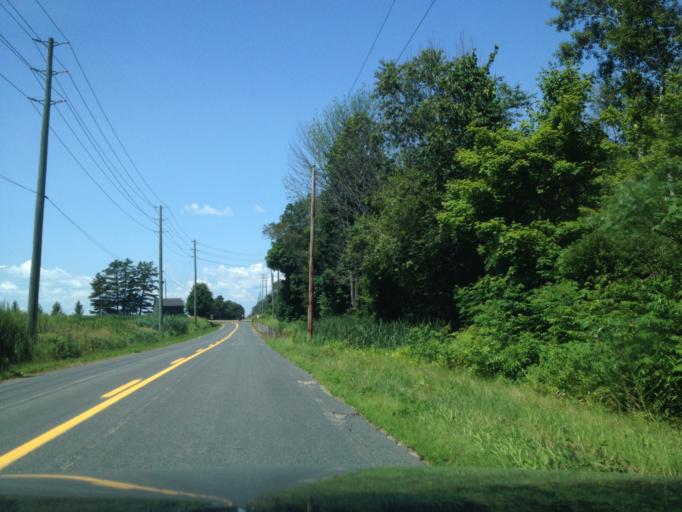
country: CA
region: Ontario
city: Aylmer
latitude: 42.6479
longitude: -80.7575
